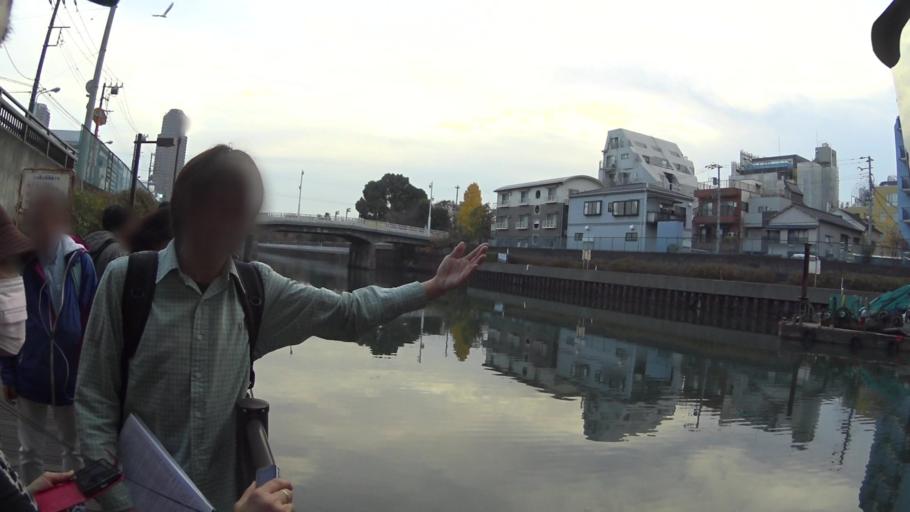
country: JP
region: Tokyo
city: Urayasu
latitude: 35.6931
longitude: 139.8200
